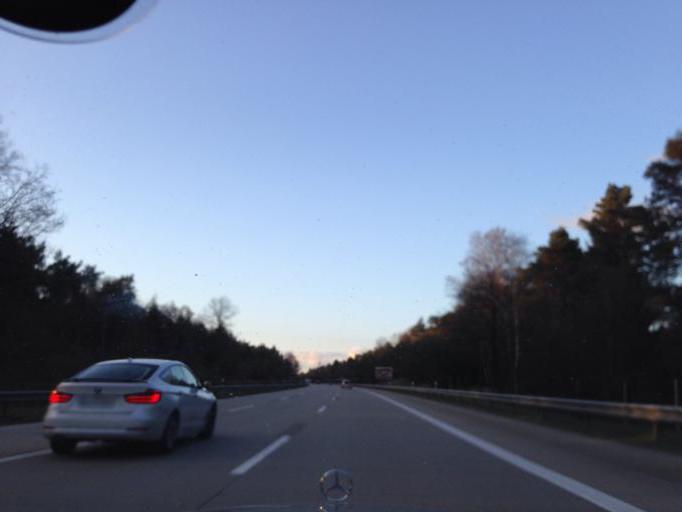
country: DE
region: Lower Saxony
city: Bispingen
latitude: 53.0408
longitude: 9.9510
